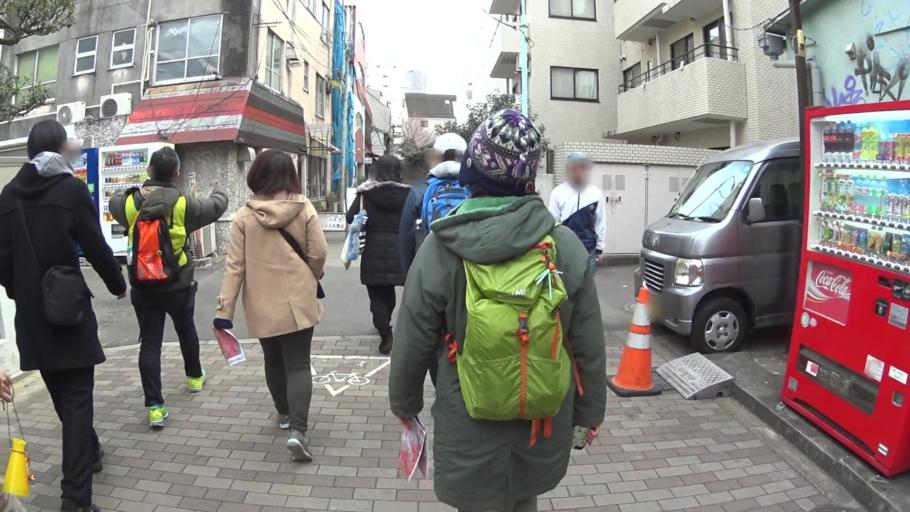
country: JP
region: Tokyo
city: Tokyo
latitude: 35.6639
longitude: 139.6941
